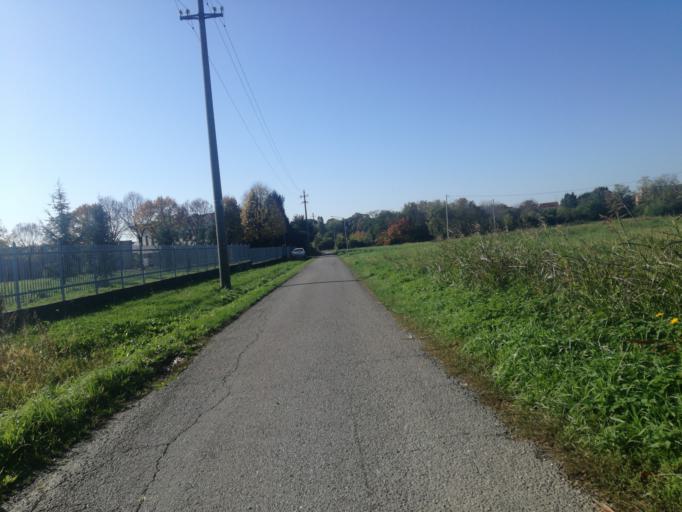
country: IT
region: Lombardy
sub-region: Provincia di Monza e Brianza
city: Porto d'Adda
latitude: 45.6513
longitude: 9.4734
